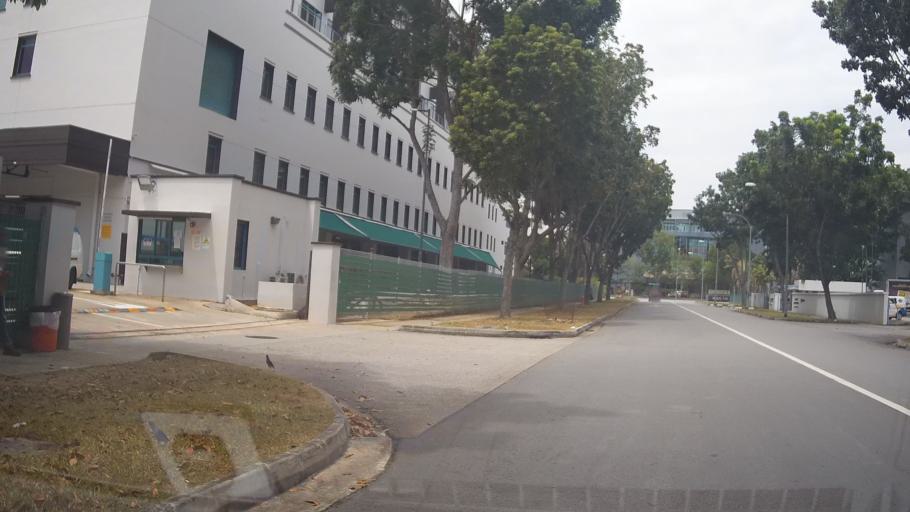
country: SG
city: Singapore
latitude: 1.3299
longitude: 103.9674
